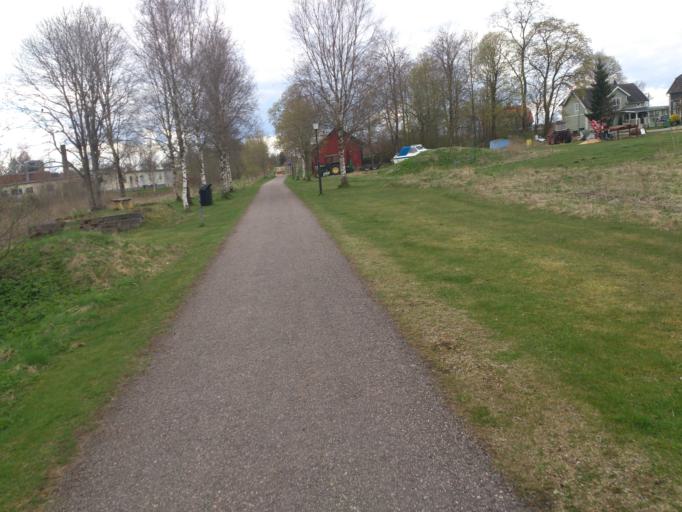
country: SE
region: Vaestra Goetaland
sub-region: Falkopings Kommun
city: Falkoeping
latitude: 57.9862
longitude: 13.5304
